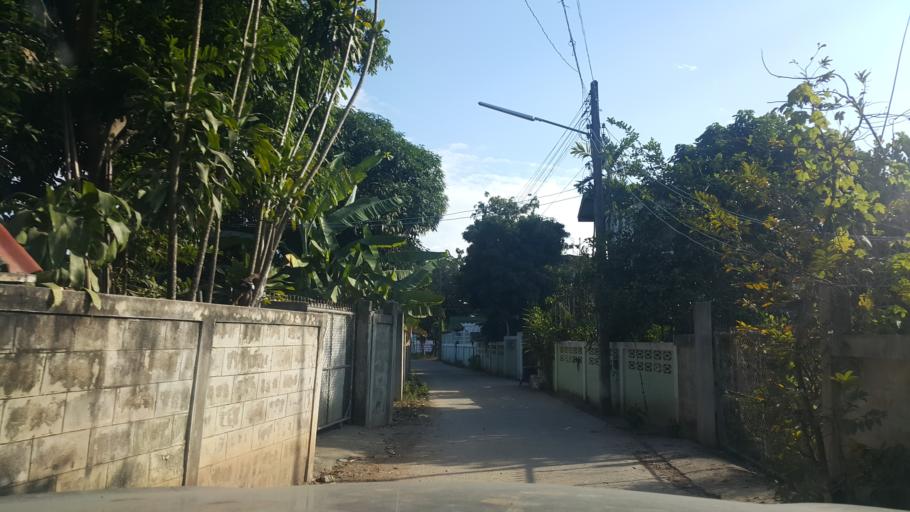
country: TH
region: Lampang
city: Hang Chat
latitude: 18.3132
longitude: 99.3520
